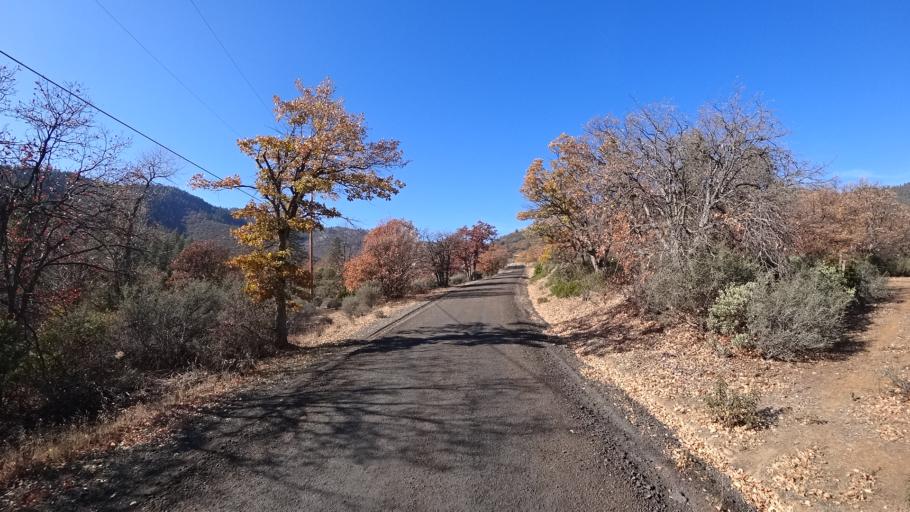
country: US
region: California
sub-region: Siskiyou County
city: Yreka
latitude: 41.7744
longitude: -122.6496
